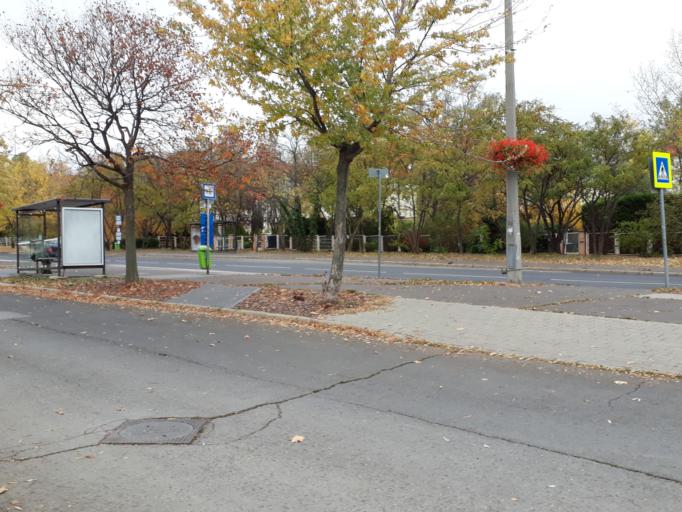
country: HU
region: Budapest
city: Budapest XII. keruelet
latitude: 47.4734
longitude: 18.9963
